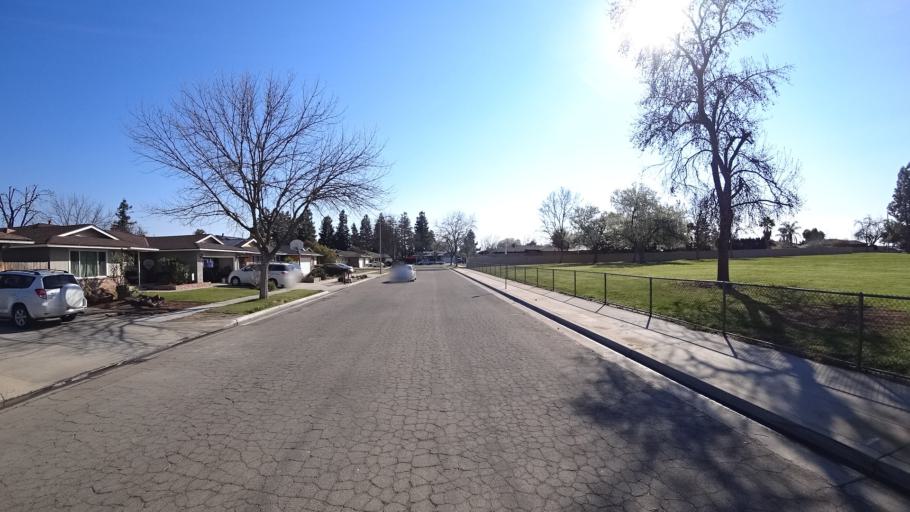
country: US
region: California
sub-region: Fresno County
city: Clovis
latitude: 36.8316
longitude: -119.7533
